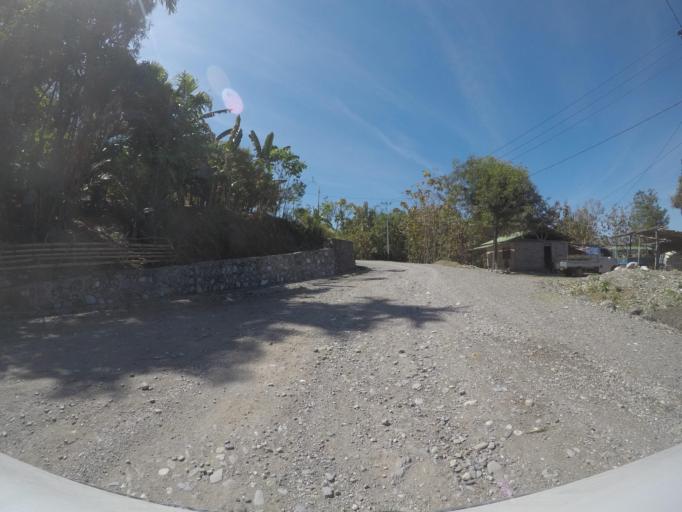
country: TL
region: Ermera
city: Gleno
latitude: -8.8081
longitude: 125.3161
